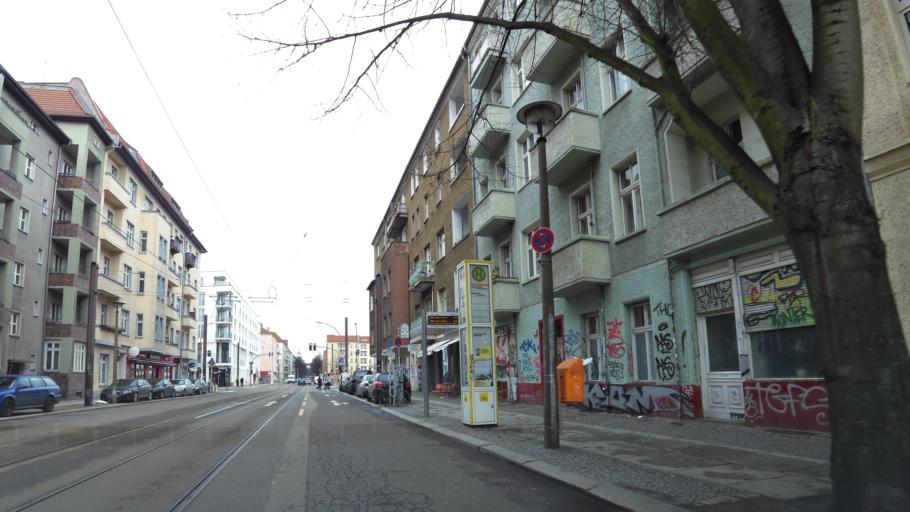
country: DE
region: Berlin
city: Friedrichshain Bezirk
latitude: 52.5080
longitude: 13.4657
